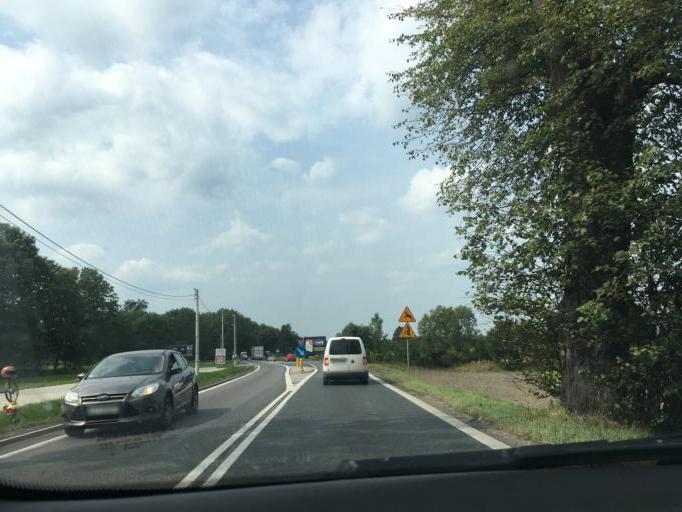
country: PL
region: Silesian Voivodeship
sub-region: Powiat bierunsko-ledzinski
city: Bierun
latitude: 50.0840
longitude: 19.1290
